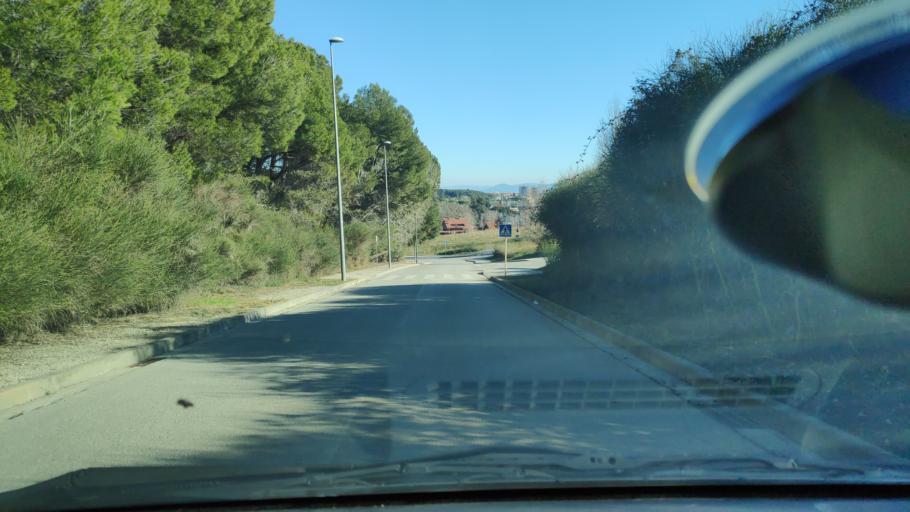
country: ES
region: Catalonia
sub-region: Provincia de Barcelona
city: Sant Quirze del Valles
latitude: 41.5380
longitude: 2.0568
